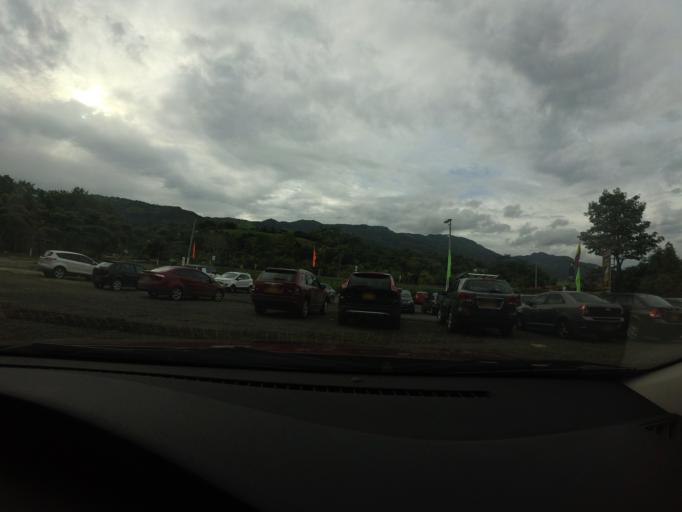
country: CO
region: Cundinamarca
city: Villeta
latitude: 5.0395
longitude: -74.4531
